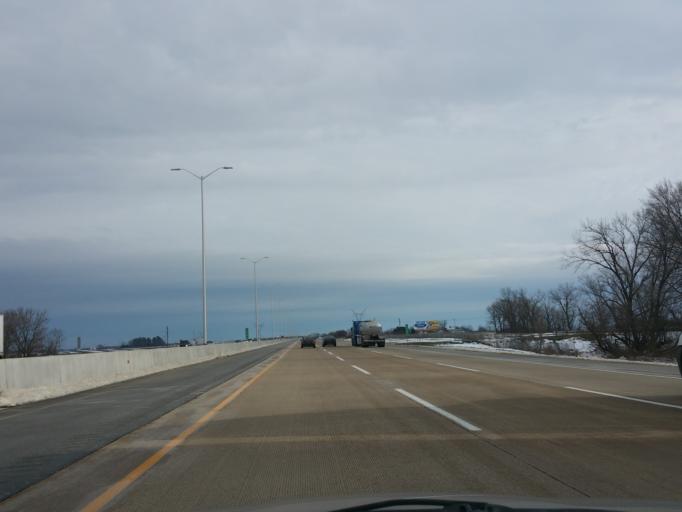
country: US
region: Illinois
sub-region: DeKalb County
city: Genoa
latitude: 42.2108
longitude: -88.7197
